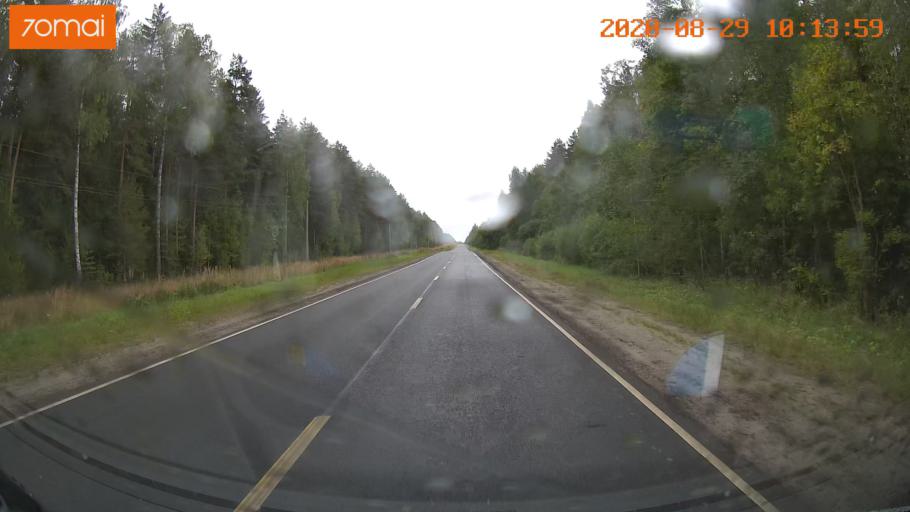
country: RU
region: Ivanovo
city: Yur'yevets
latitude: 57.3576
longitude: 42.7442
